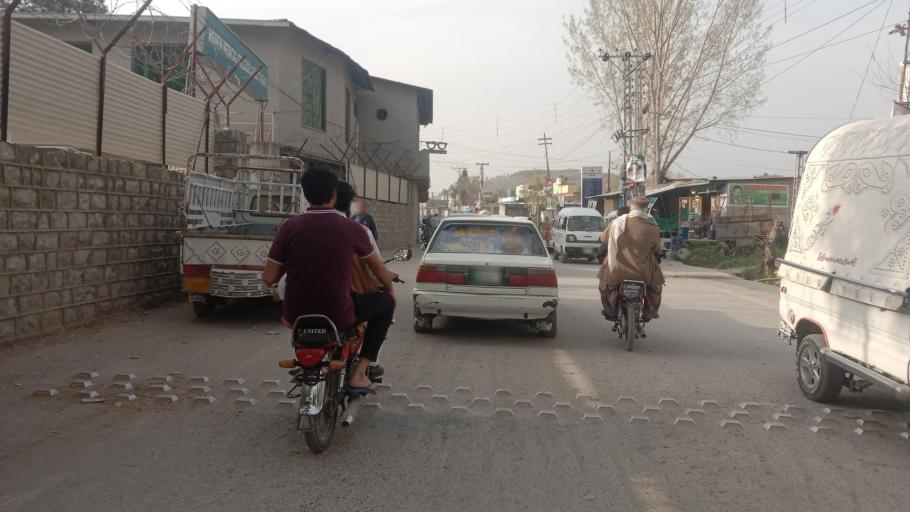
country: PK
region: Khyber Pakhtunkhwa
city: Abbottabad
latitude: 34.1603
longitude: 73.2637
